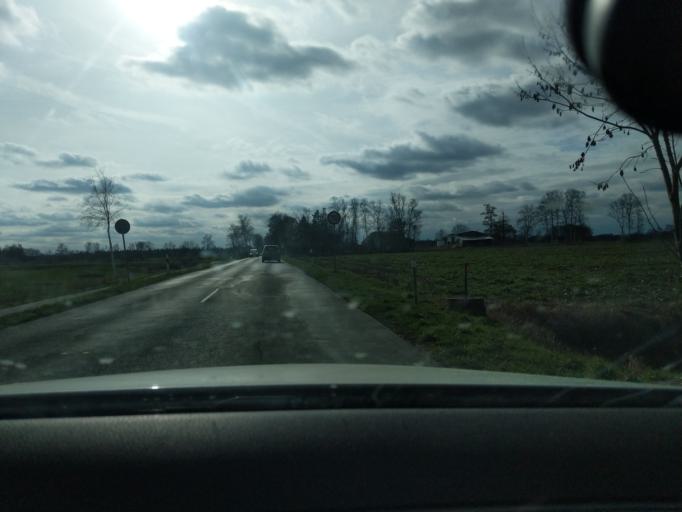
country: DE
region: Lower Saxony
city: Hammah
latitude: 53.6504
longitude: 9.3666
